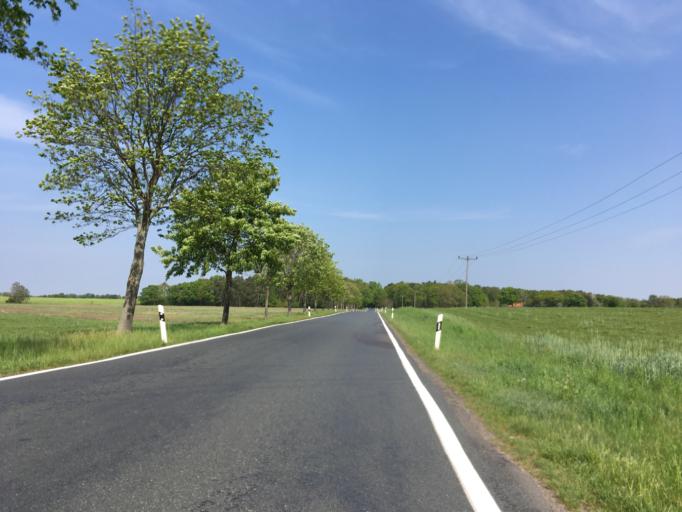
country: DE
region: Brandenburg
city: Melchow
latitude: 52.7197
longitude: 13.7131
